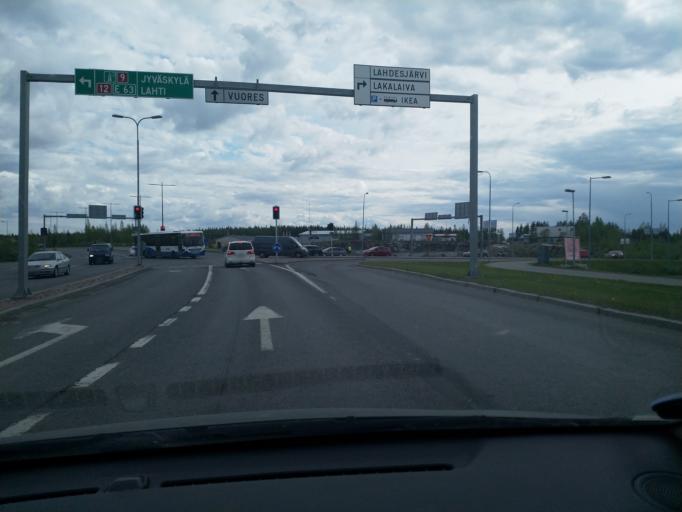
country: FI
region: Pirkanmaa
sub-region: Tampere
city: Tampere
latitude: 61.4595
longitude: 23.7905
